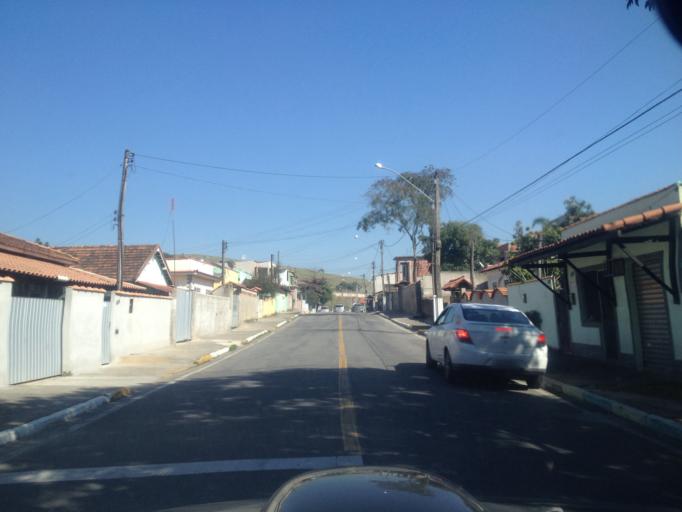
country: BR
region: Rio de Janeiro
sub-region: Porto Real
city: Porto Real
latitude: -22.4471
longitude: -44.3075
